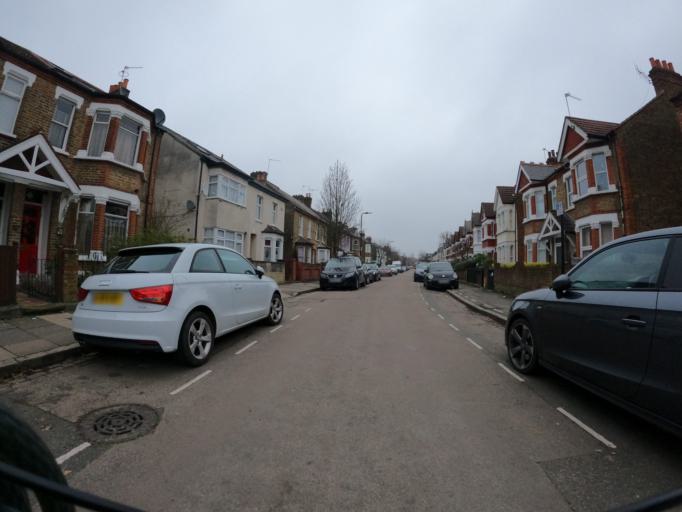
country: GB
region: England
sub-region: Greater London
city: Ealing
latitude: 51.5060
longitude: -0.3295
